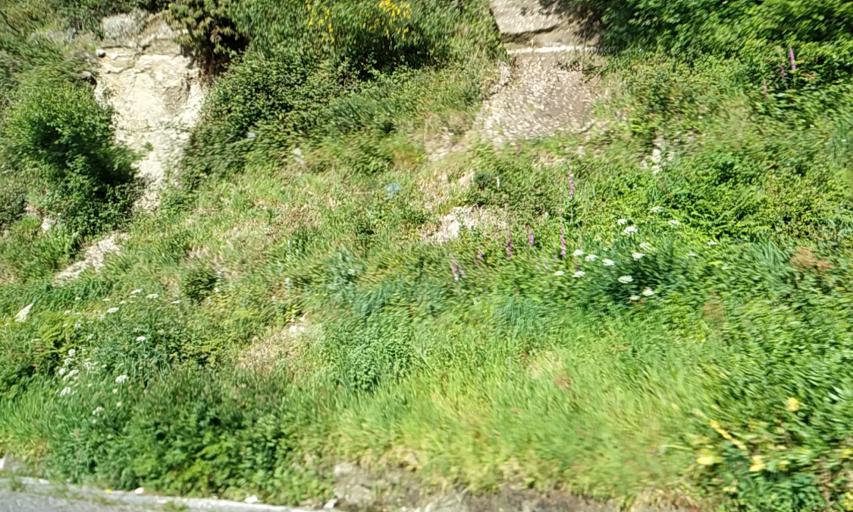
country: ES
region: Galicia
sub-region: Provincia de Pontevedra
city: Meano
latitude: 42.4629
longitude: -8.7786
